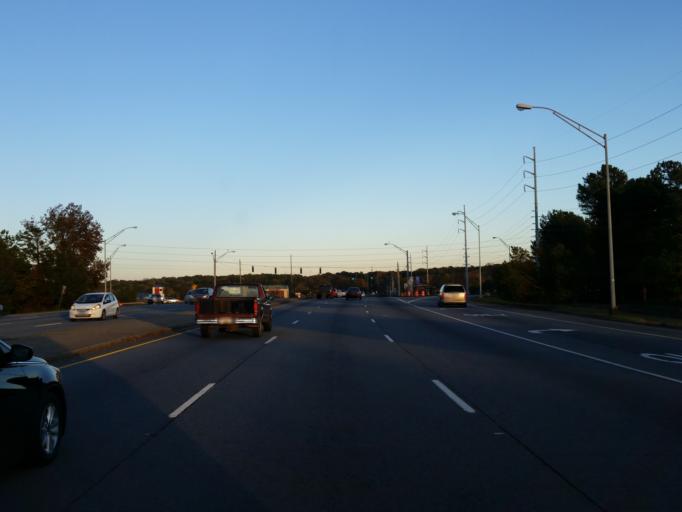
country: US
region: Georgia
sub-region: Cobb County
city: Smyrna
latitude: 33.9227
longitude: -84.4882
